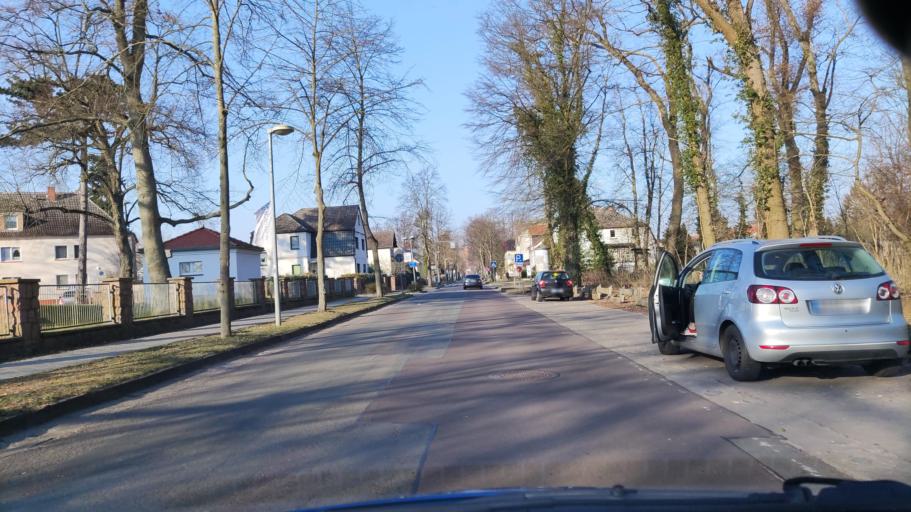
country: DE
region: Saxony-Anhalt
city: Seehausen
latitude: 52.8817
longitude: 11.7479
